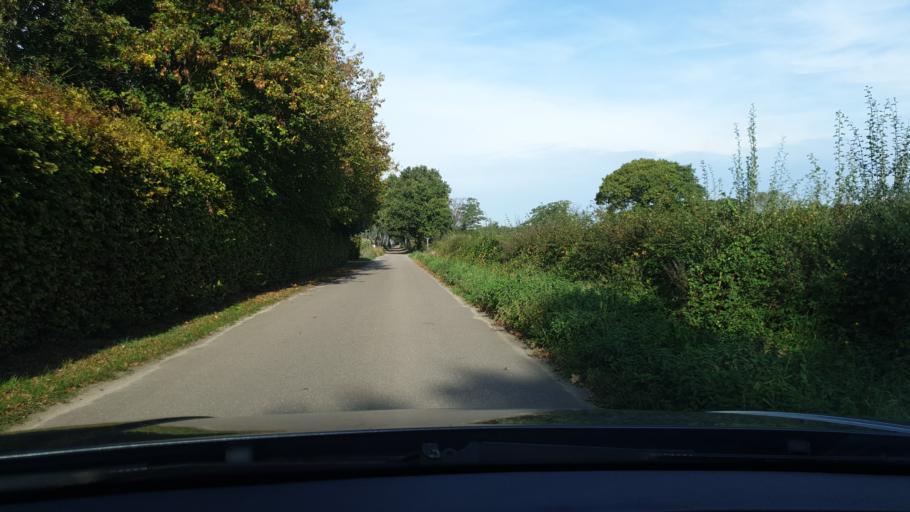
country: BE
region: Flanders
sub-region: Provincie Antwerpen
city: Laakdal
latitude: 51.1249
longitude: 5.0258
